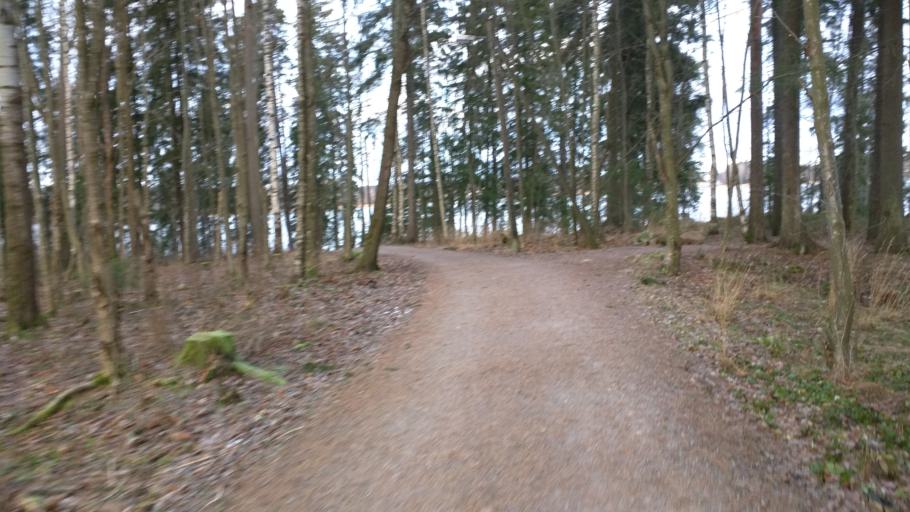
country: FI
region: Uusimaa
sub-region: Helsinki
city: Kauniainen
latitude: 60.2475
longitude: 24.7484
